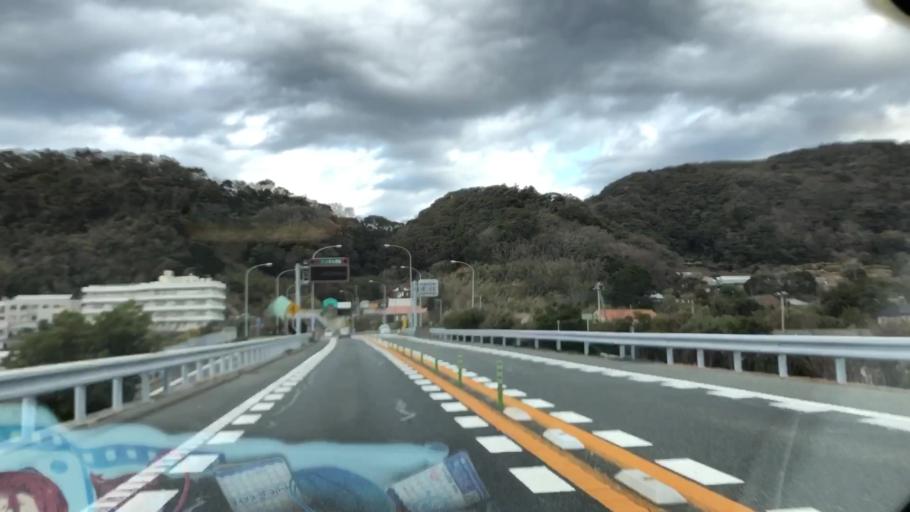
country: JP
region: Chiba
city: Tateyama
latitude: 35.1428
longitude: 139.8478
